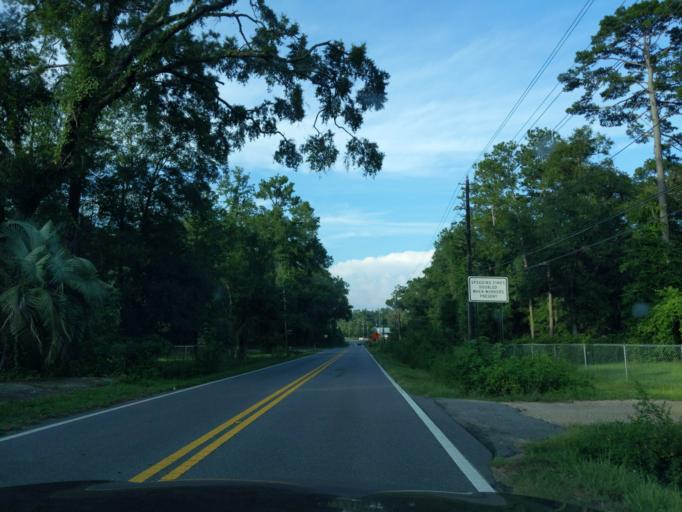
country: US
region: Florida
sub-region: Leon County
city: Tallahassee
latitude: 30.4023
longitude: -84.3103
